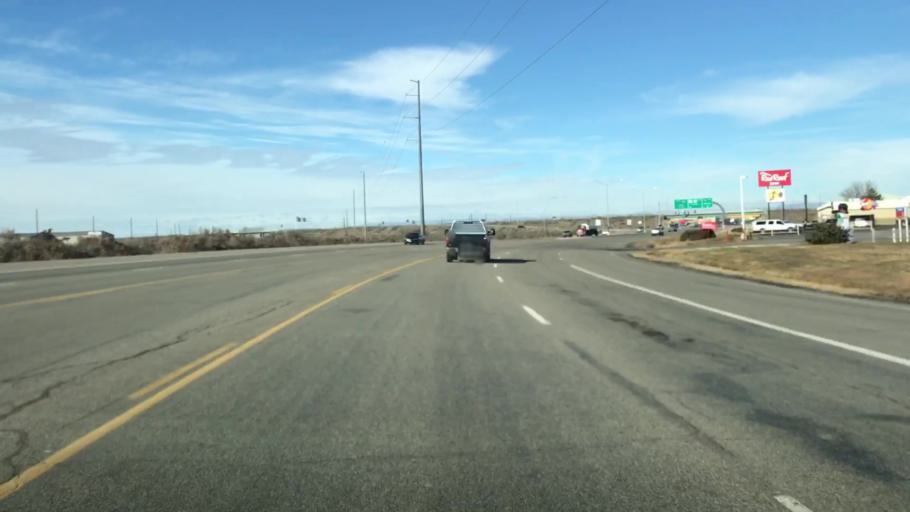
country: US
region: Colorado
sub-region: Mesa County
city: Redlands
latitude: 39.1082
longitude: -108.6411
